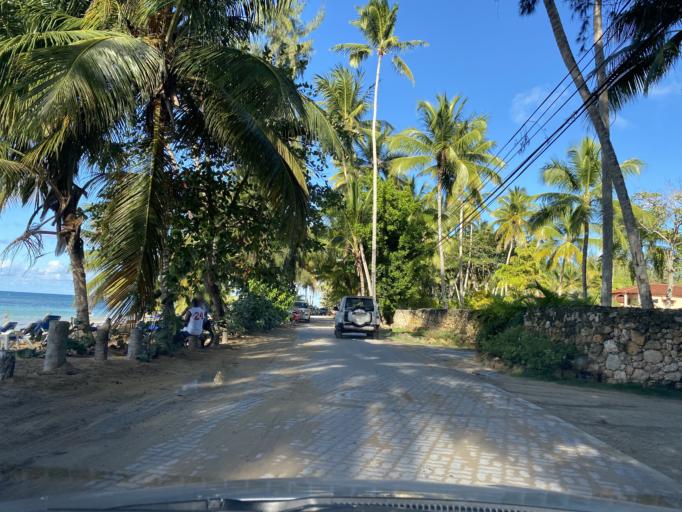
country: DO
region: Samana
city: Las Terrenas
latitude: 19.3232
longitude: -69.5535
